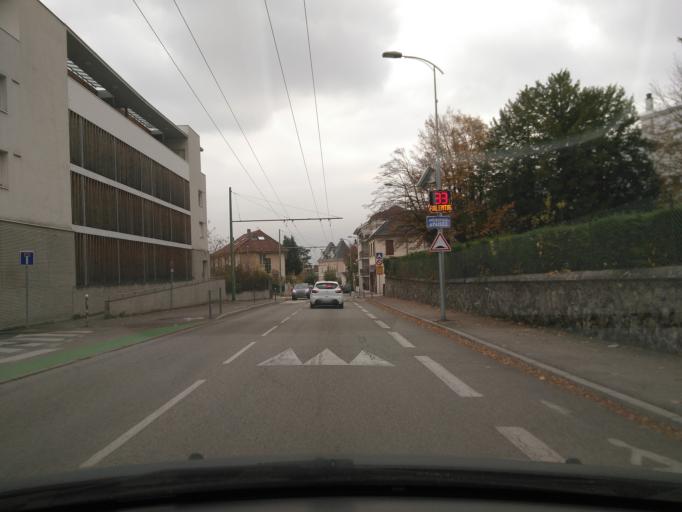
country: FR
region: Rhone-Alpes
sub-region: Departement de l'Isere
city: La Tronche
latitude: 45.2051
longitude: 5.7479
